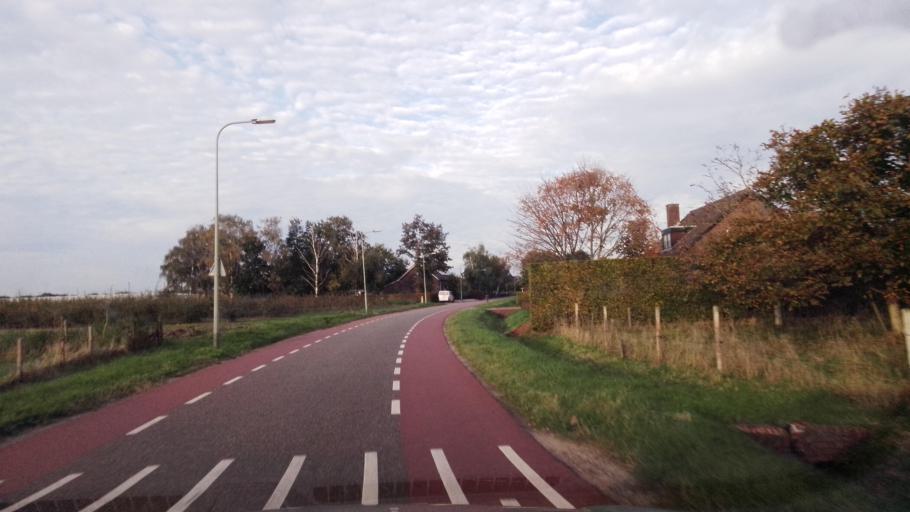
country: NL
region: Limburg
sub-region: Gemeente Venlo
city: Tegelen
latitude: 51.3219
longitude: 6.1319
